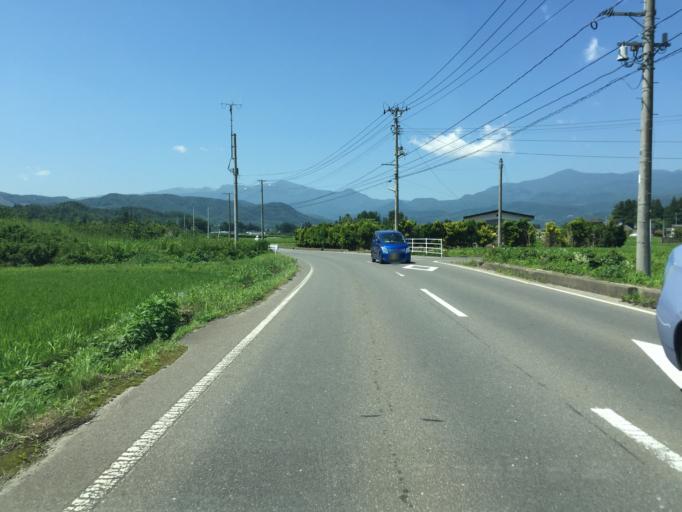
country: JP
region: Fukushima
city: Fukushima-shi
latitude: 37.7256
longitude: 140.4053
